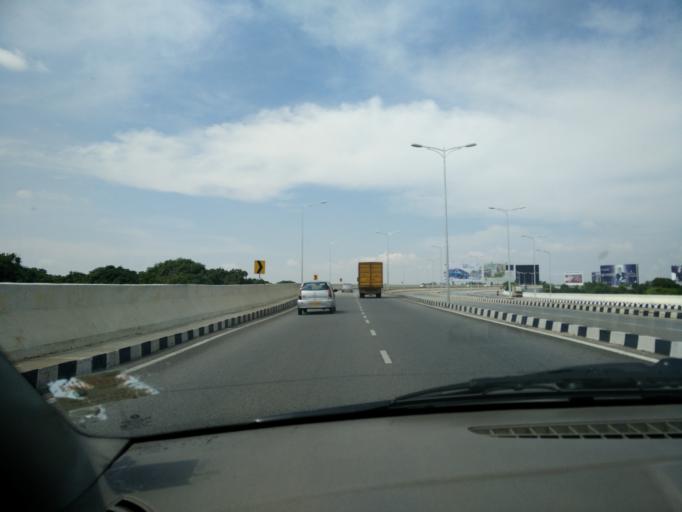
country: IN
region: Karnataka
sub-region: Bangalore Rural
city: Devanhalli
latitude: 13.1981
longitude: 77.6659
